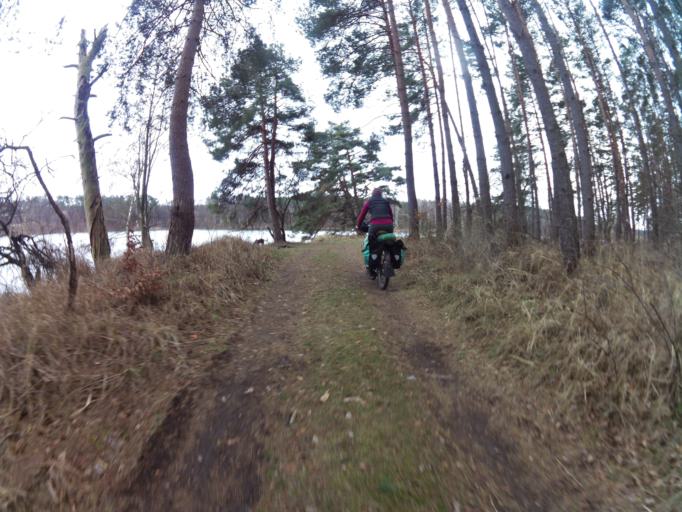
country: PL
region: West Pomeranian Voivodeship
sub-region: Powiat mysliborski
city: Debno
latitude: 52.7654
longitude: 14.8086
